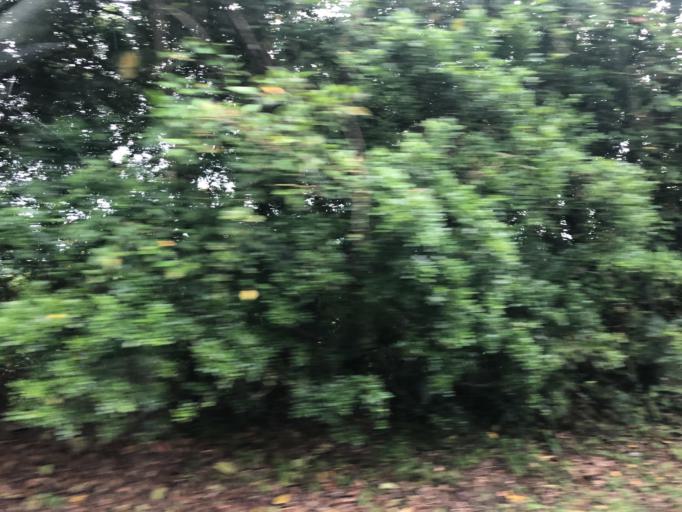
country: TW
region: Taiwan
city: Daxi
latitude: 24.8857
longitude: 121.4188
